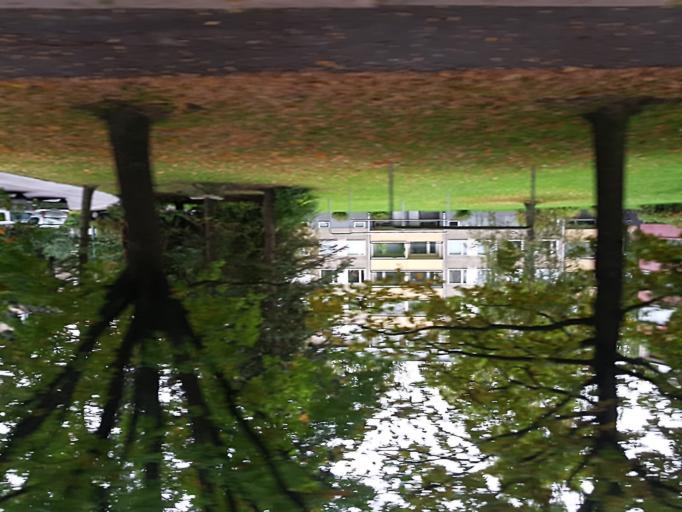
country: FI
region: Uusimaa
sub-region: Helsinki
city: Teekkarikylae
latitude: 60.2422
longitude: 24.8768
